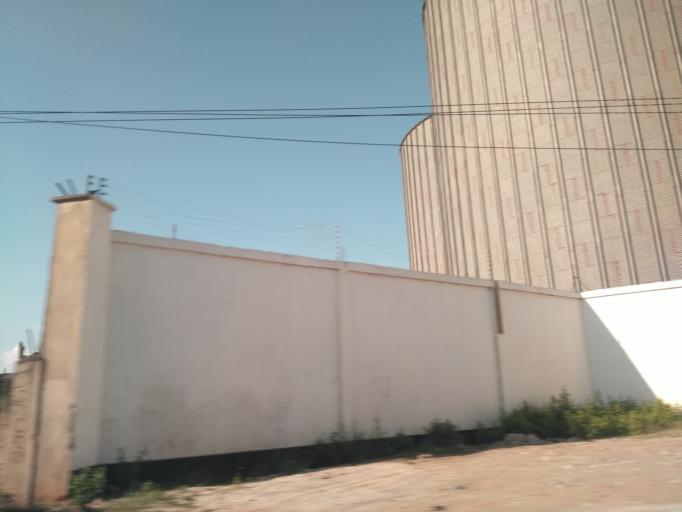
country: TZ
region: Dar es Salaam
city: Magomeni
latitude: -6.7595
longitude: 39.2372
